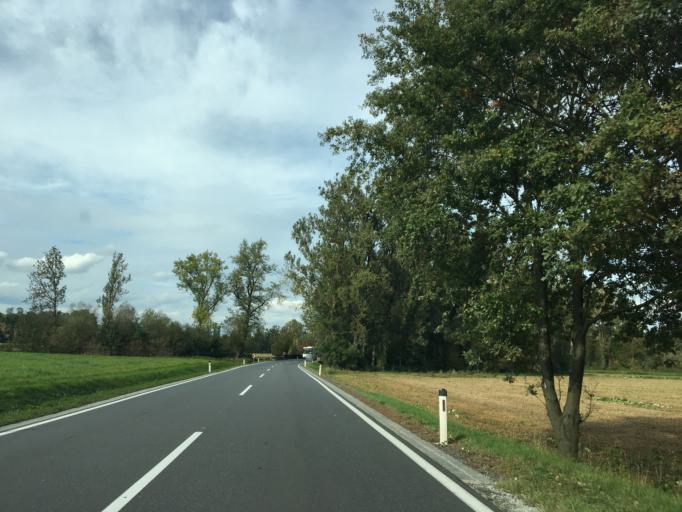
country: AT
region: Upper Austria
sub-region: Wels-Land
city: Buchkirchen
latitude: 48.2752
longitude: 13.9950
